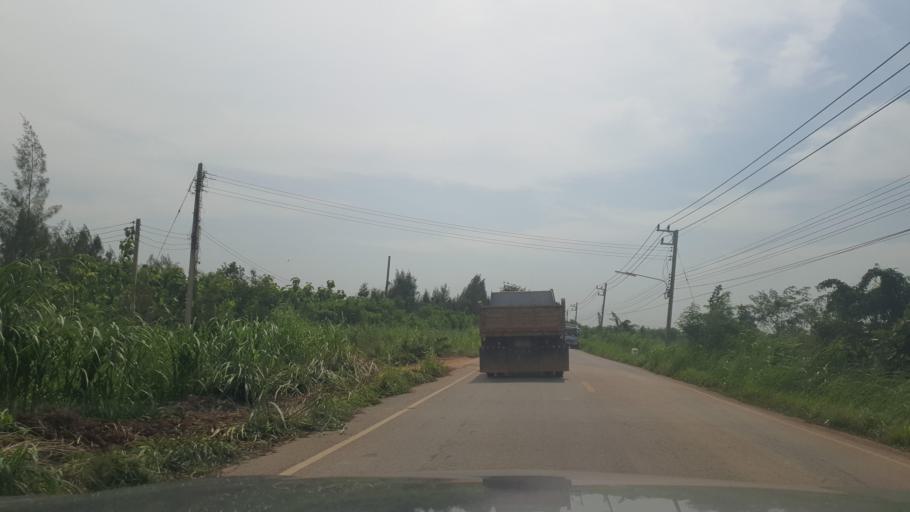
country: TH
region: Sukhothai
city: Si Samrong
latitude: 17.1177
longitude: 99.8737
